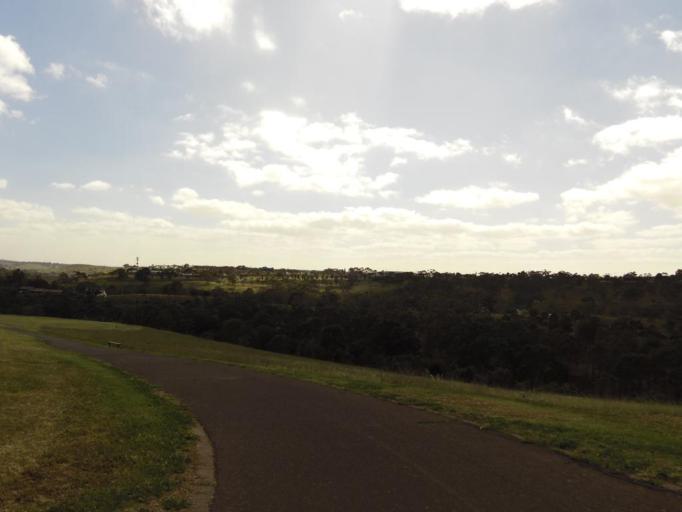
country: AU
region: Victoria
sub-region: Brimbank
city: Kealba
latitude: -37.7322
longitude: 144.8409
